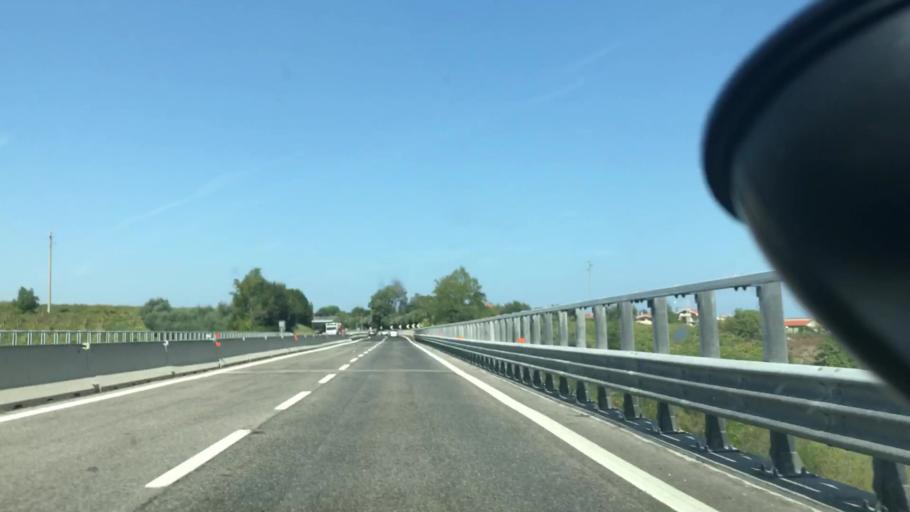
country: IT
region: Abruzzo
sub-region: Provincia di Chieti
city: Tollo
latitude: 42.3549
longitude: 14.3518
